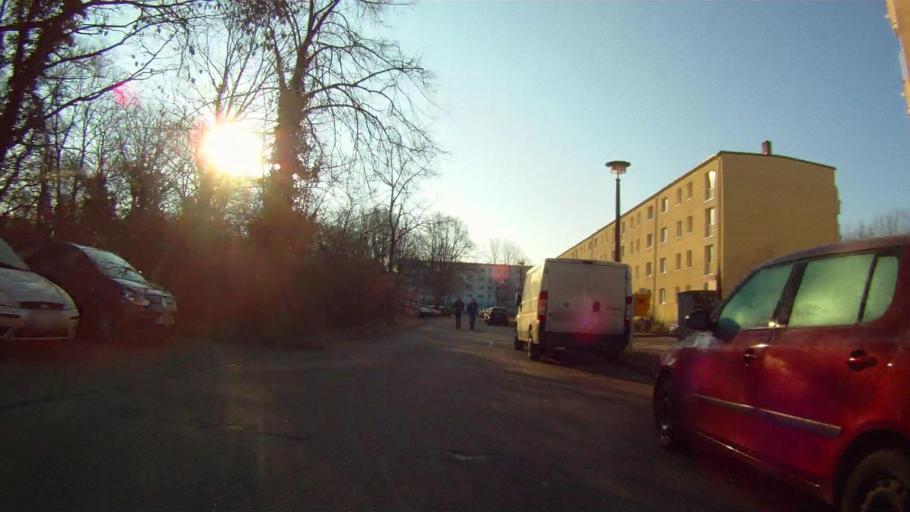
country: DE
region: Berlin
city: Kopenick Bezirk
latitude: 52.4420
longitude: 13.5634
